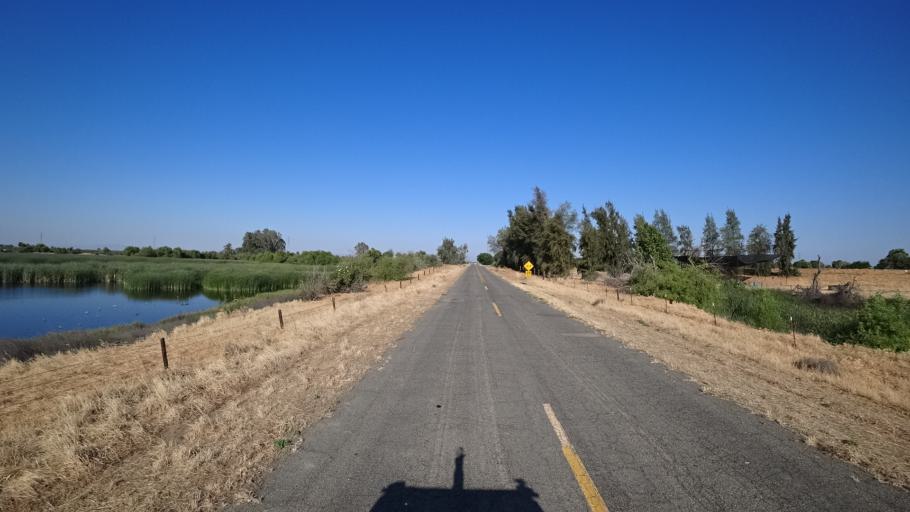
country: US
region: California
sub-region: Fresno County
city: Riverdale
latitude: 36.3766
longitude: -119.8822
